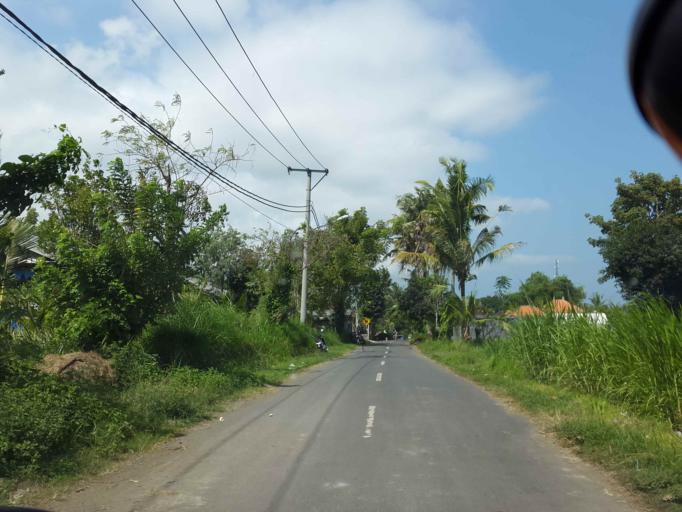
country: ID
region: Bali
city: Klungkung
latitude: -8.5441
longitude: 115.3720
